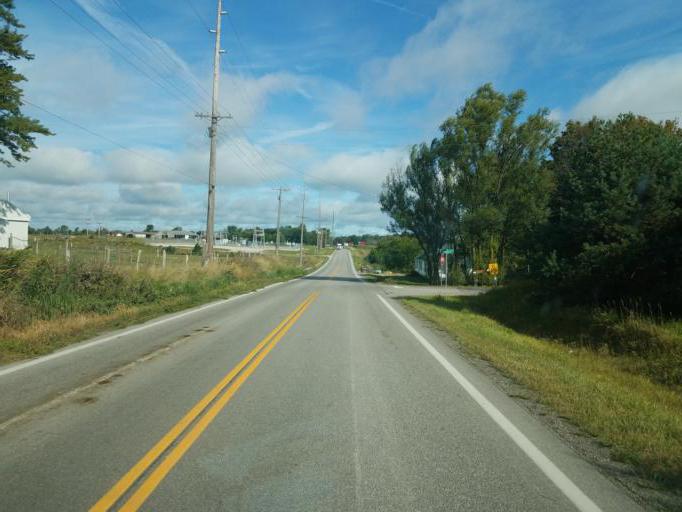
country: US
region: Ohio
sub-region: Wayne County
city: West Salem
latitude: 41.0165
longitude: -82.1204
